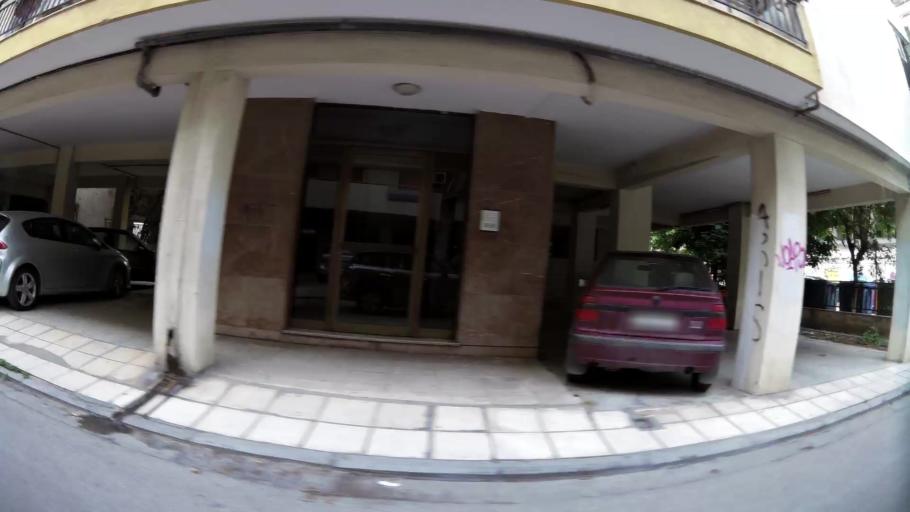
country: GR
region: Central Macedonia
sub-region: Nomos Thessalonikis
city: Kalamaria
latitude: 40.5895
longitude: 22.9640
